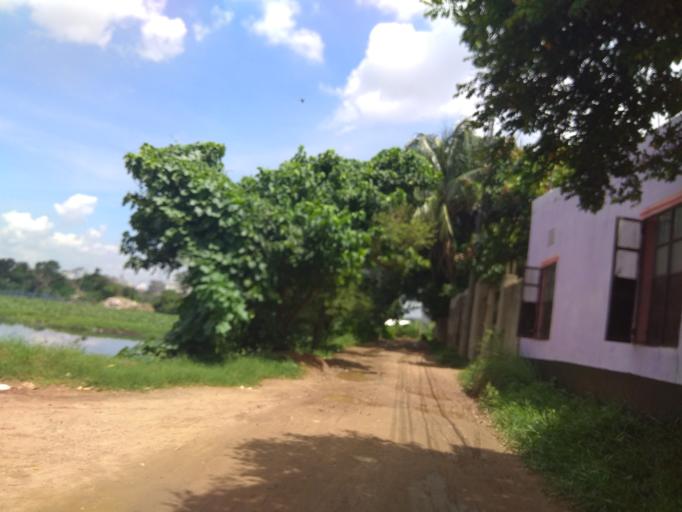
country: BD
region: Dhaka
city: Tungi
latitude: 23.8265
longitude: 90.3842
